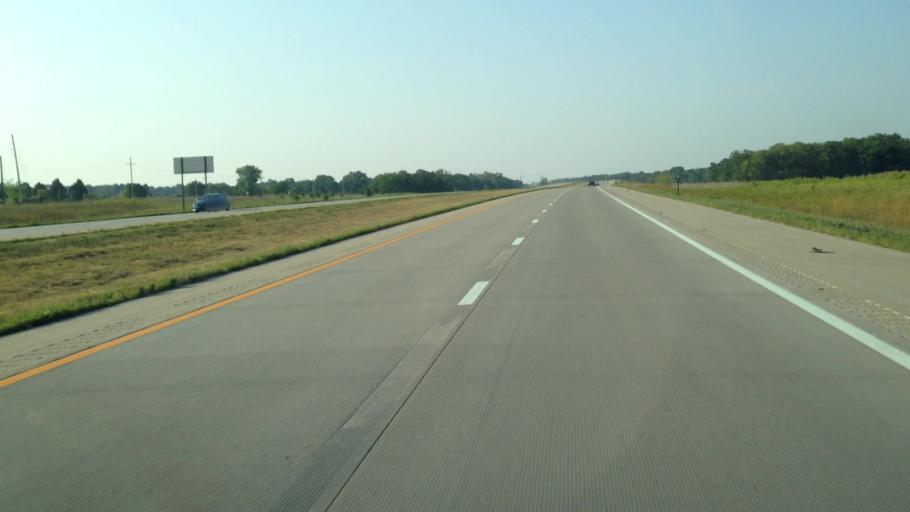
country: US
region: Kansas
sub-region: Douglas County
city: Baldwin City
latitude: 38.7298
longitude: -95.2682
